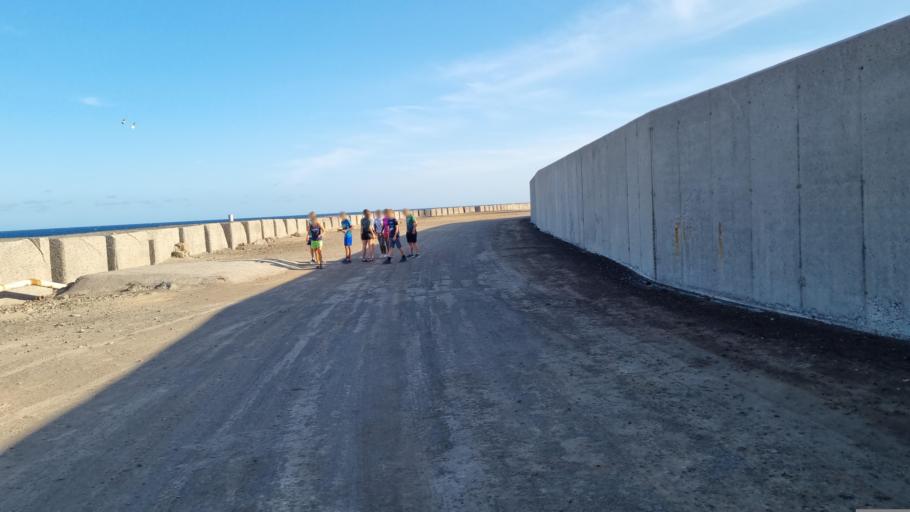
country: ES
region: Canary Islands
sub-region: Provincia de Santa Cruz de Tenerife
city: San Isidro
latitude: 28.0872
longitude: -16.4907
